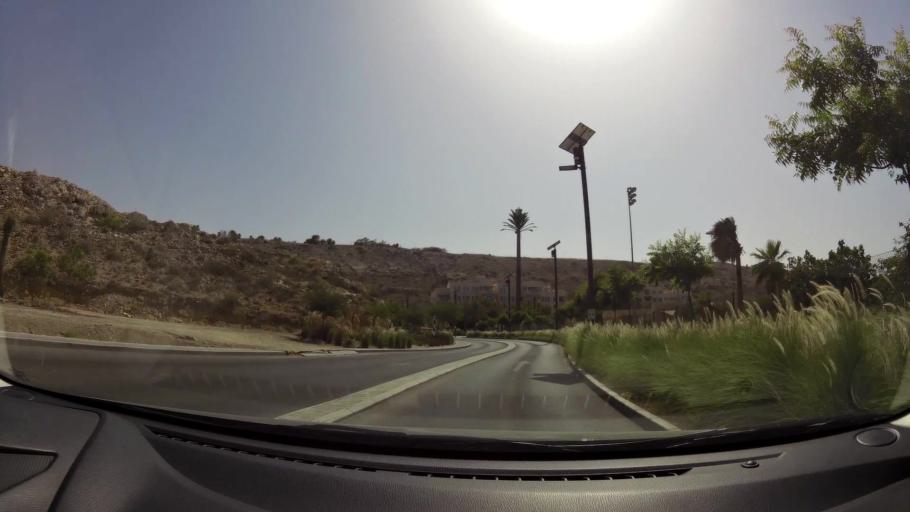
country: OM
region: Muhafazat Masqat
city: Muscat
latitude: 23.6345
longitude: 58.5019
